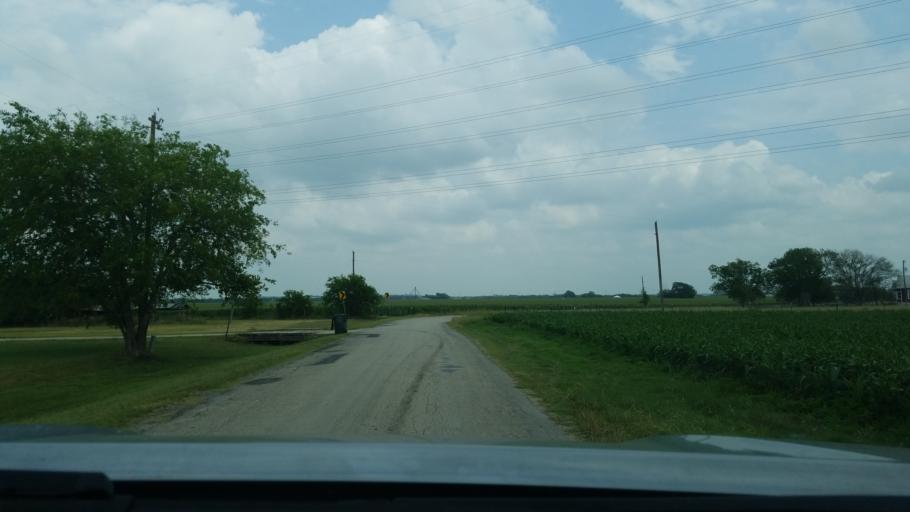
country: US
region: Texas
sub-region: Guadalupe County
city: Geronimo
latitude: 29.6796
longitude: -98.0159
